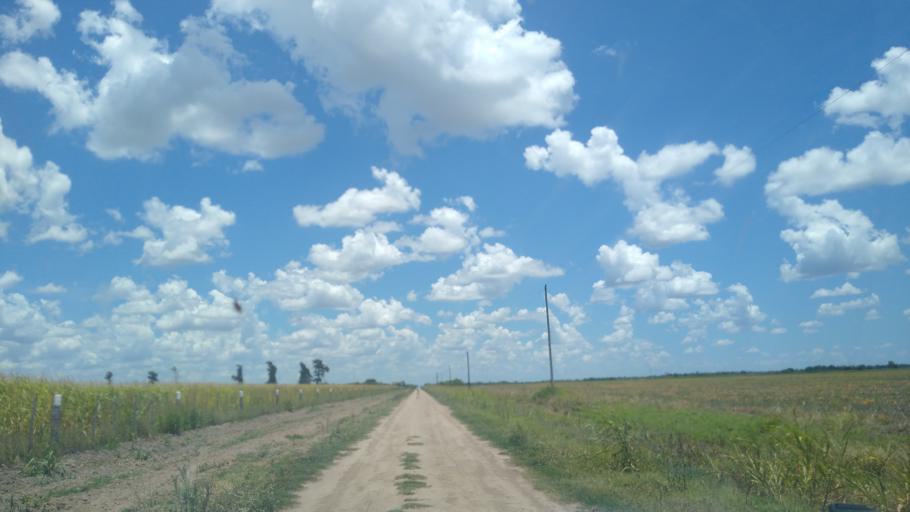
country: AR
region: Chaco
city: Presidencia Roque Saenz Pena
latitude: -26.7429
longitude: -60.3516
